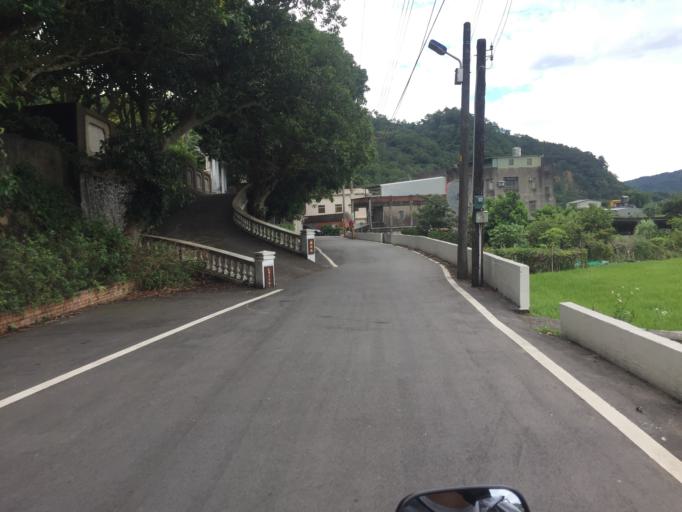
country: TW
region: Taiwan
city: Daxi
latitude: 24.7894
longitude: 121.1674
